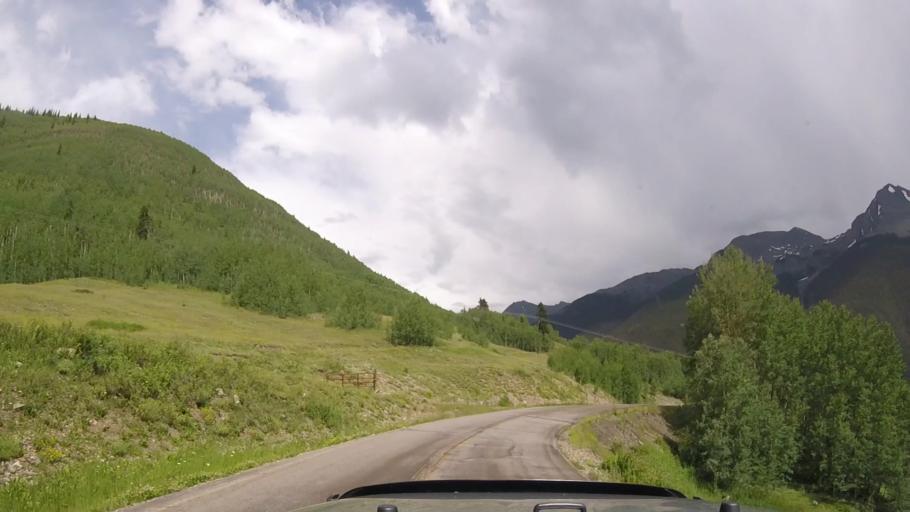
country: US
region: Colorado
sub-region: San Juan County
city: Silverton
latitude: 37.8207
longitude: -107.6621
